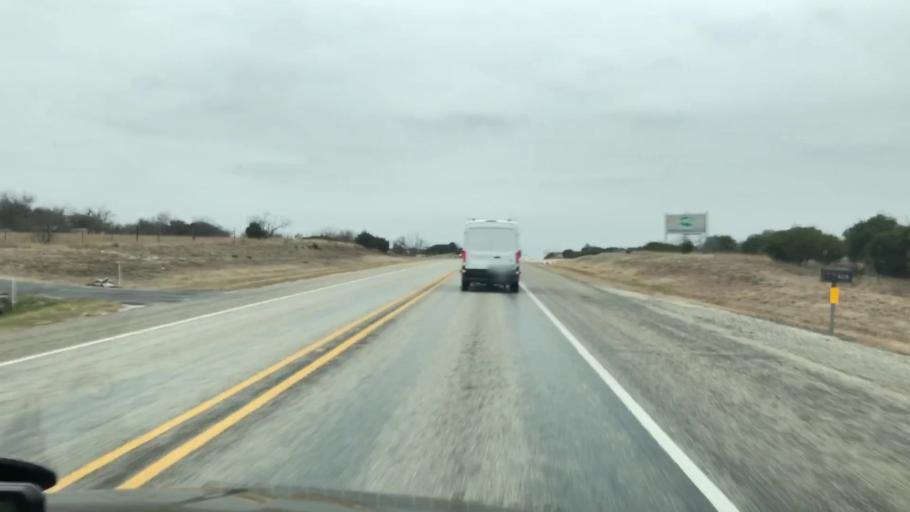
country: US
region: Texas
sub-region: Lampasas County
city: Lampasas
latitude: 31.1229
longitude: -98.1909
